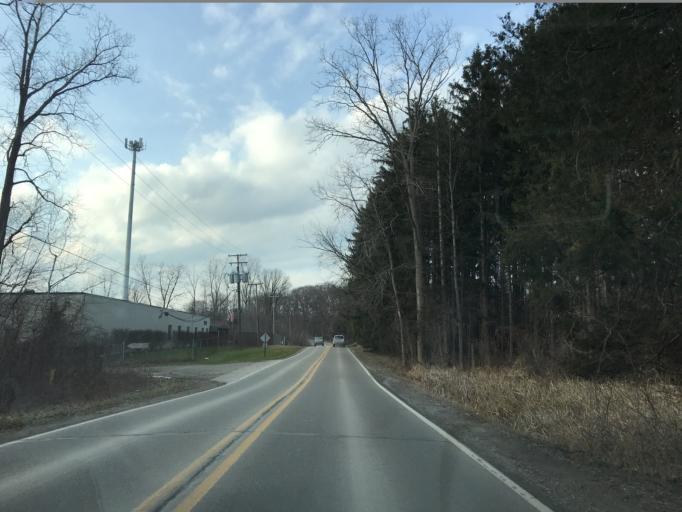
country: US
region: Michigan
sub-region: Oakland County
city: South Lyon
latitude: 42.4666
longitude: -83.6978
